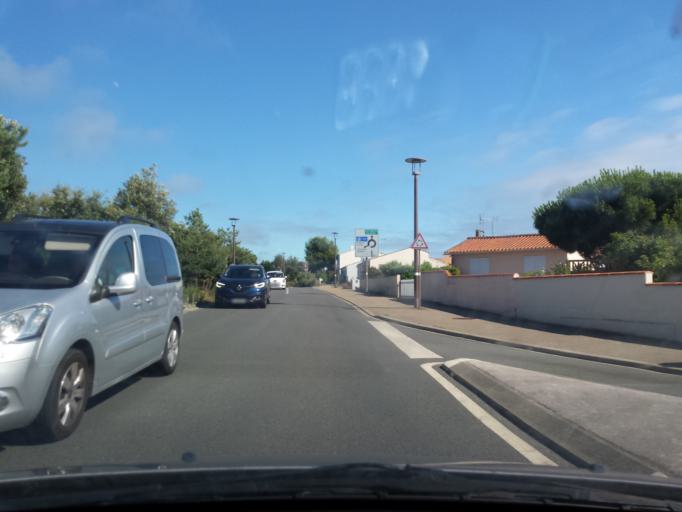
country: FR
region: Pays de la Loire
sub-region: Departement de la Vendee
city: Bretignolles-sur-Mer
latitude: 46.6253
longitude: -1.8544
